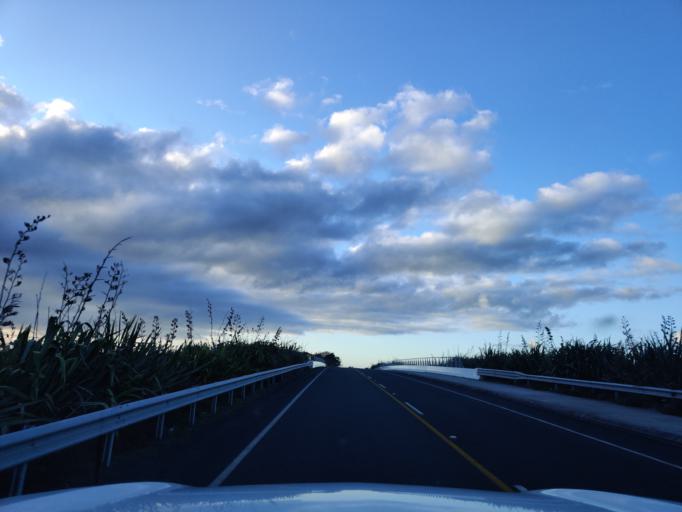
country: NZ
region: Waikato
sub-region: Waipa District
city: Cambridge
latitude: -37.8695
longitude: 175.4390
